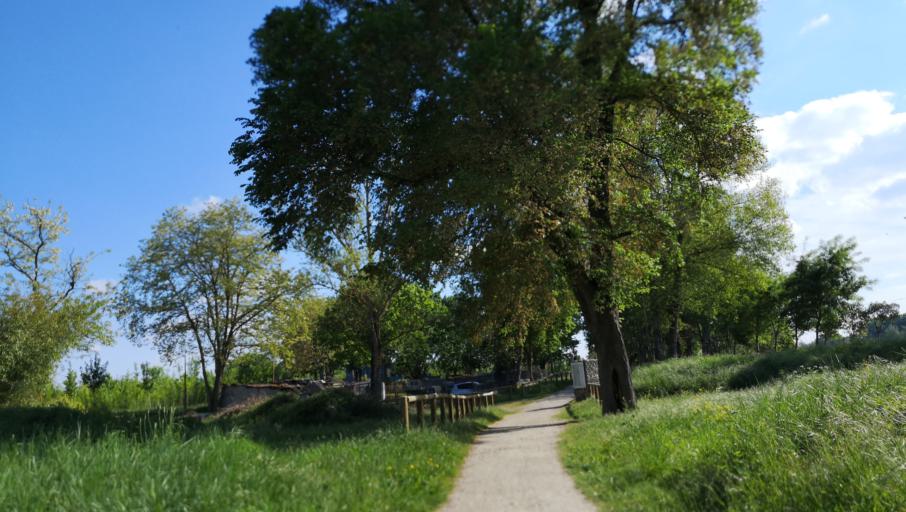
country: FR
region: Midi-Pyrenees
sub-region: Departement de la Haute-Garonne
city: Blagnac
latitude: 43.6335
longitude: 1.4048
